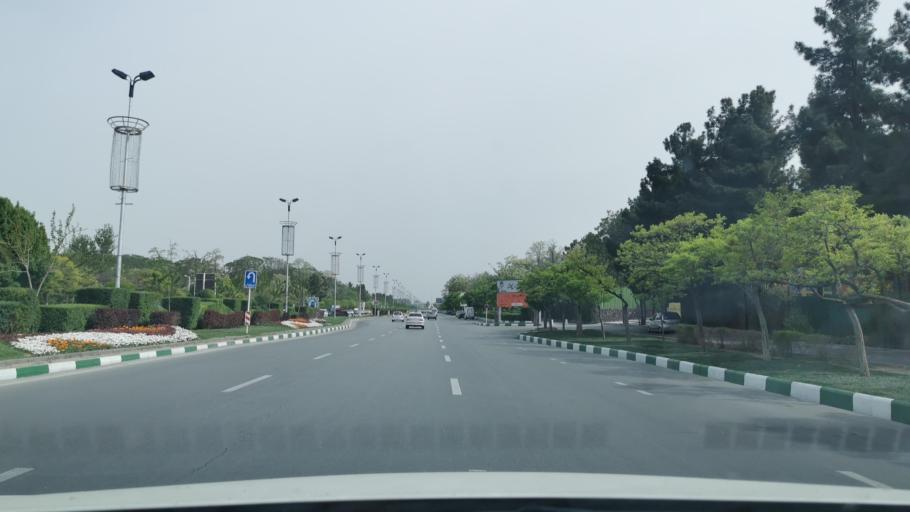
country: IR
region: Razavi Khorasan
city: Mashhad
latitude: 36.2515
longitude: 59.6150
